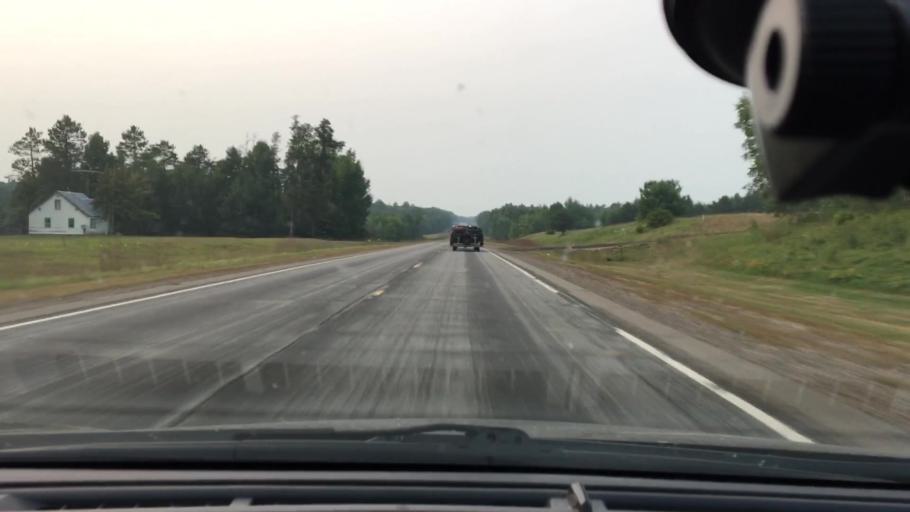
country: US
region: Minnesota
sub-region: Crow Wing County
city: Cross Lake
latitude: 46.6884
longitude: -93.9541
